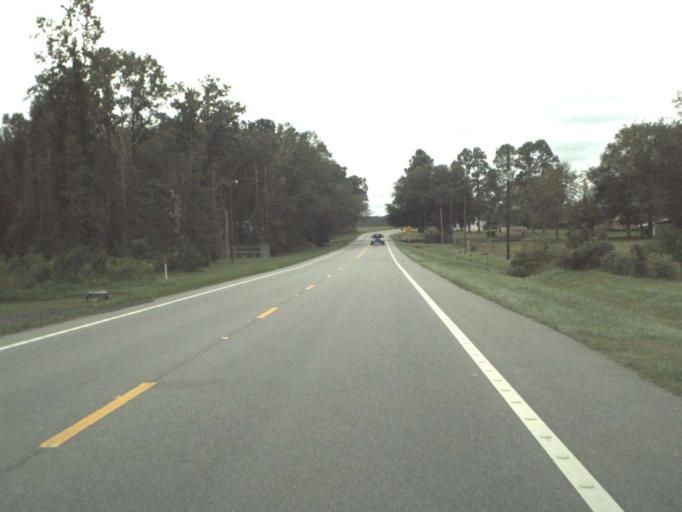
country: US
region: Florida
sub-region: Jackson County
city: Sneads
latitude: 30.6974
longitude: -85.0204
